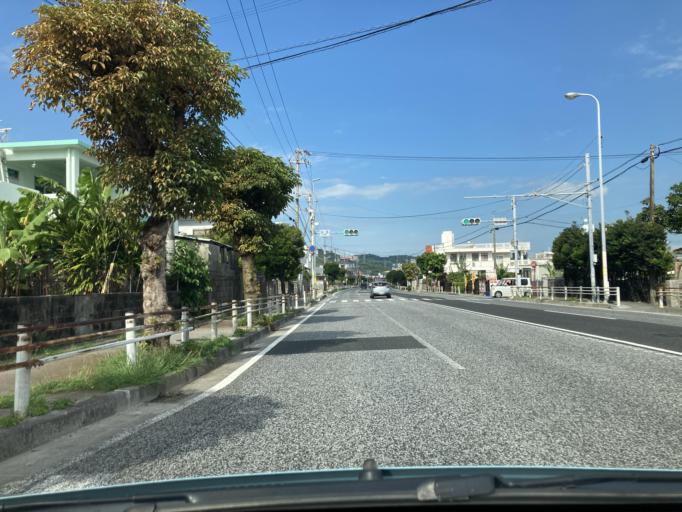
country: JP
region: Okinawa
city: Ginowan
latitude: 26.2596
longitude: 127.7868
